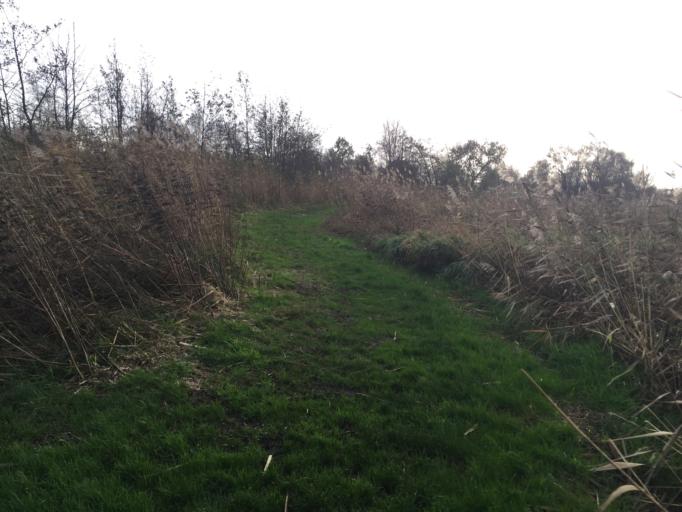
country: NL
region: North Holland
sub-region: Gemeente Ouder-Amstel
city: Ouderkerk aan de Amstel
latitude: 52.2522
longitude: 4.9392
